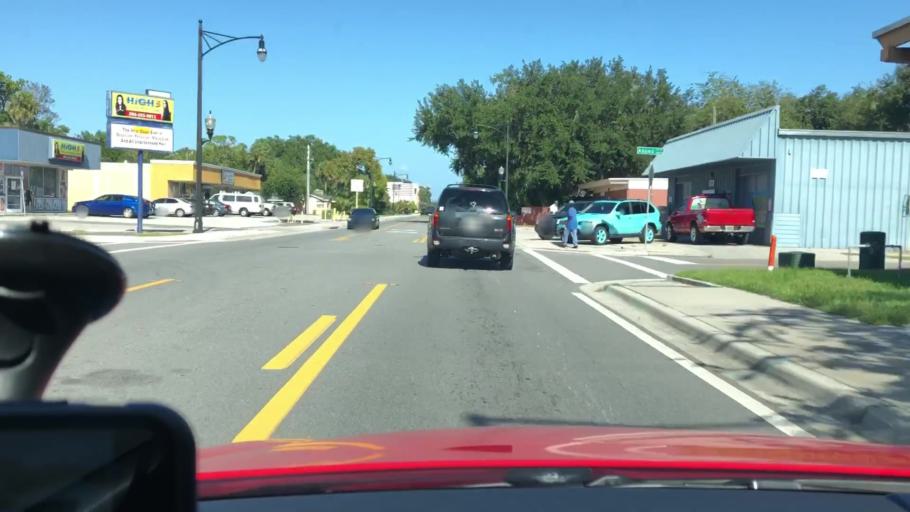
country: US
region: Florida
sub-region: Volusia County
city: Daytona Beach
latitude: 29.2015
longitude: -81.0342
